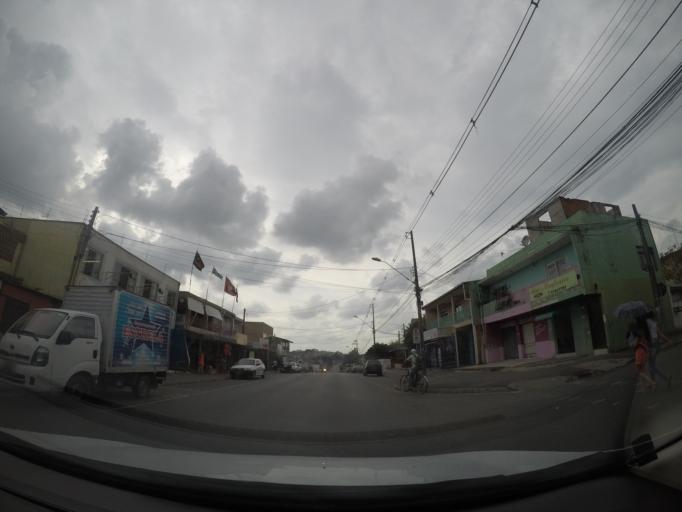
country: BR
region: Parana
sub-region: Sao Jose Dos Pinhais
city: Sao Jose dos Pinhais
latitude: -25.5504
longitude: -49.2480
